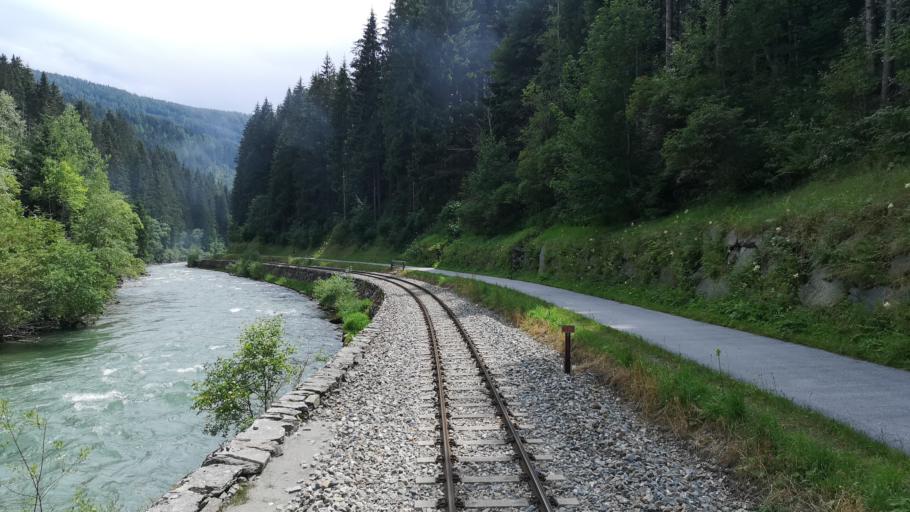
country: AT
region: Salzburg
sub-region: Politischer Bezirk Tamsweg
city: Tamsweg
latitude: 47.1035
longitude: 13.8199
